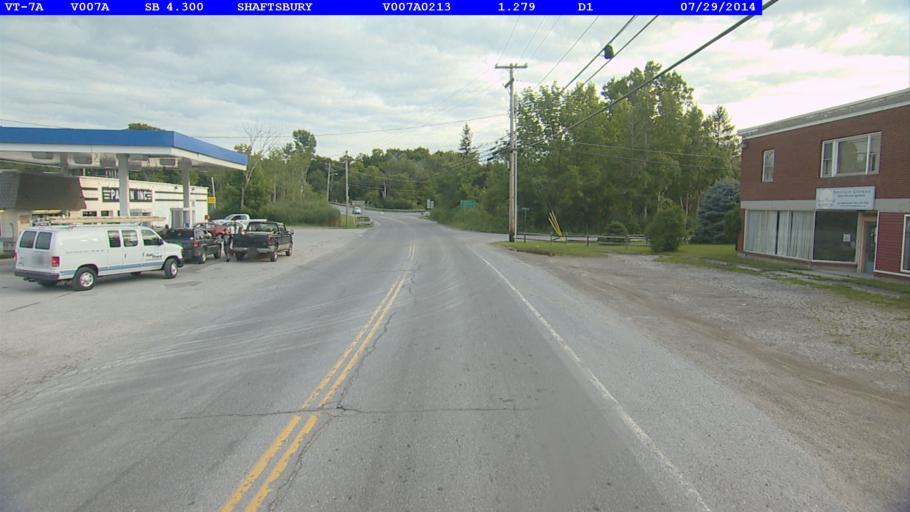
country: US
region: Vermont
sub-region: Bennington County
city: North Bennington
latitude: 42.9509
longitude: -73.2109
